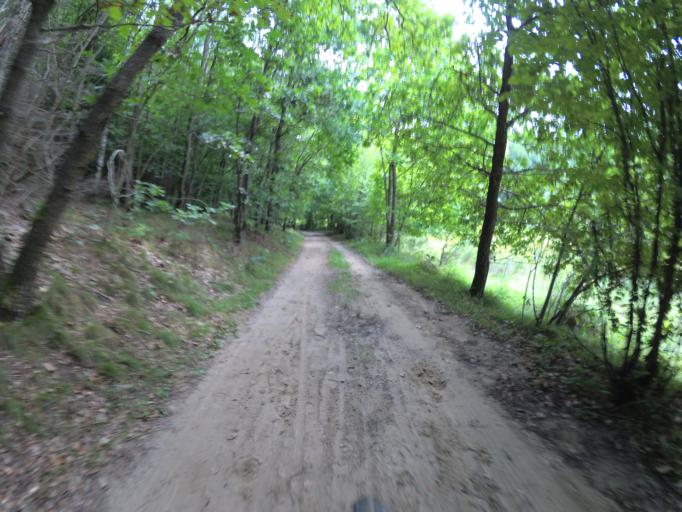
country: PL
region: Pomeranian Voivodeship
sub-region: Gdynia
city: Wielki Kack
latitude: 54.4895
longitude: 18.4456
